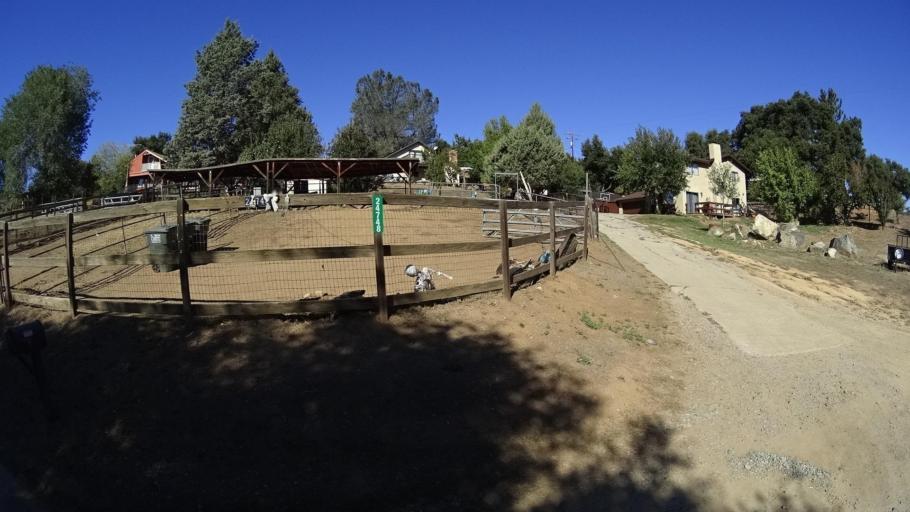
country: US
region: California
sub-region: San Diego County
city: Descanso
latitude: 32.8552
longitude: -116.6146
